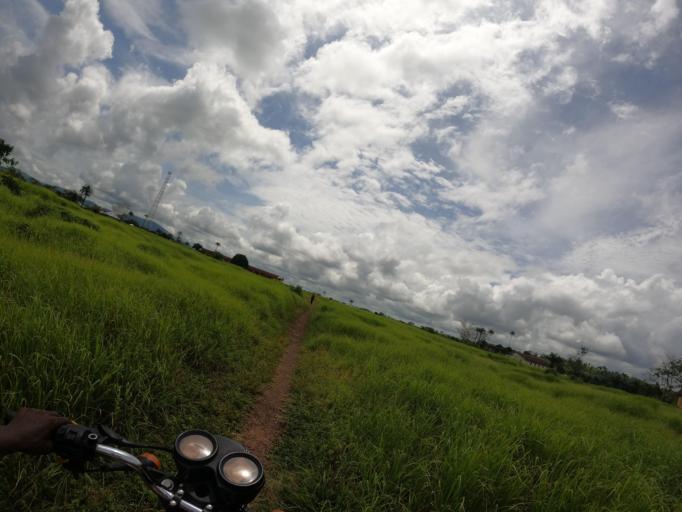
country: SL
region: Northern Province
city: Makeni
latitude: 9.1035
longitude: -12.2048
